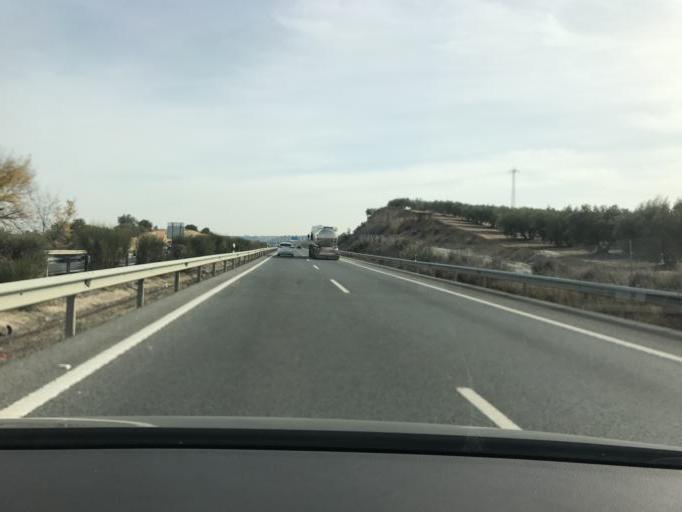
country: ES
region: Andalusia
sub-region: Provincia de Granada
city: Moraleda de Zafayona
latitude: 37.1797
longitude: -3.9162
